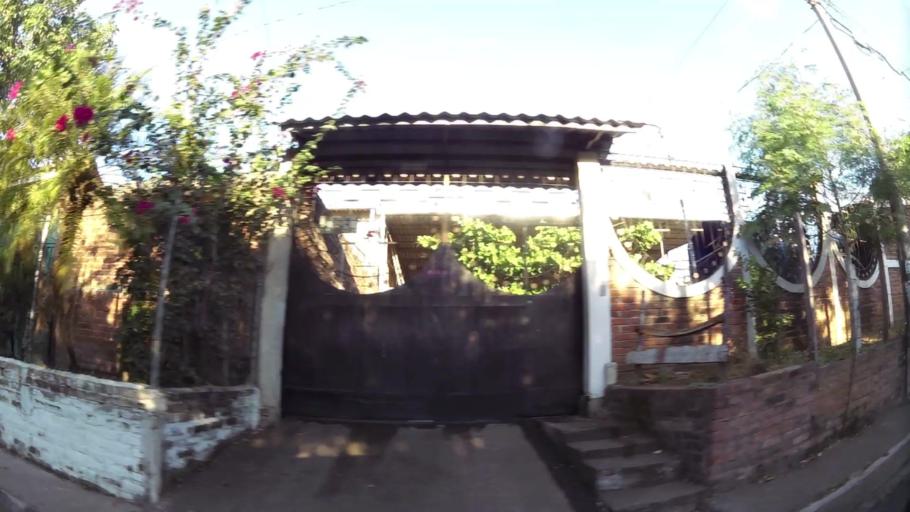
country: SV
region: Sonsonate
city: San Antonio del Monte
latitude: 13.7081
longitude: -89.7337
